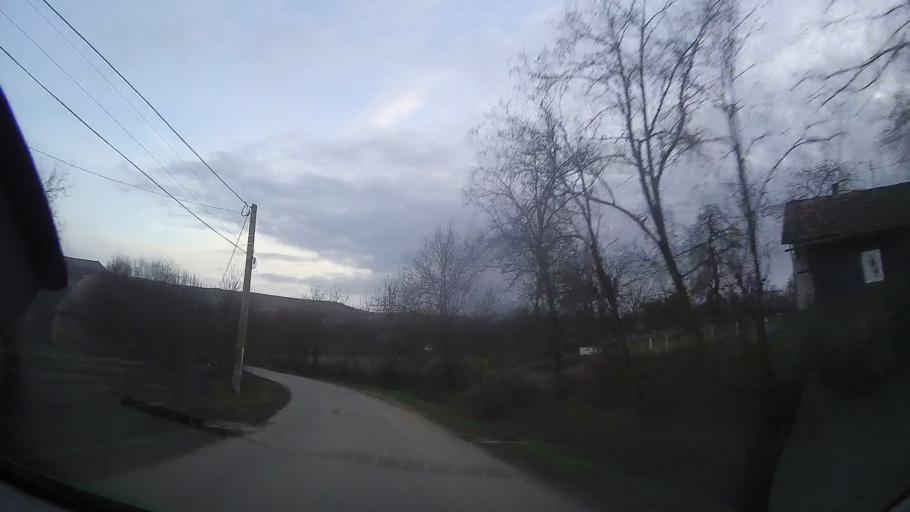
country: RO
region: Cluj
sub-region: Comuna Palatca
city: Palatca
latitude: 46.8455
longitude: 23.9906
